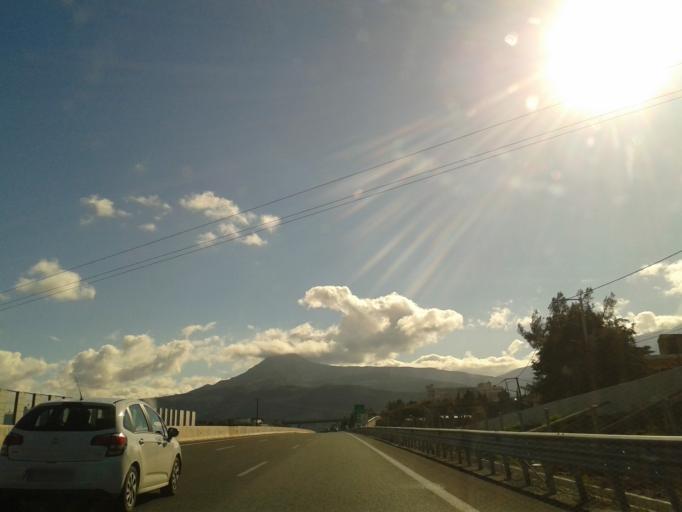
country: GR
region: West Greece
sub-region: Nomos Achaias
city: Aigio
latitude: 38.2470
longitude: 22.0721
